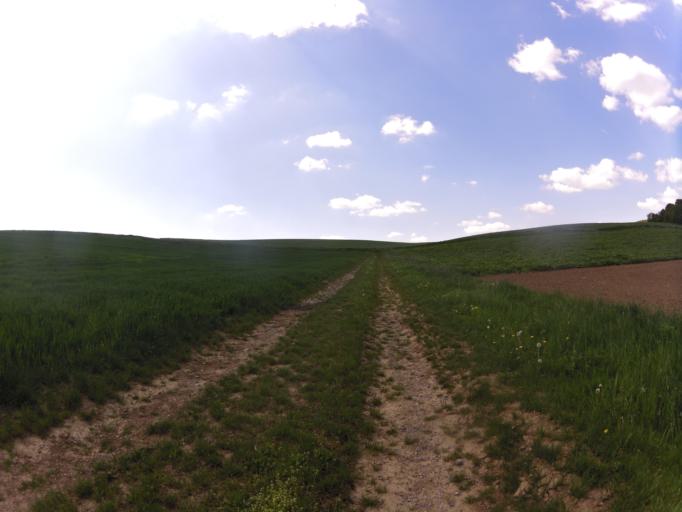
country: DE
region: Bavaria
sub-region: Regierungsbezirk Unterfranken
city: Unterpleichfeld
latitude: 49.8846
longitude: 10.0046
